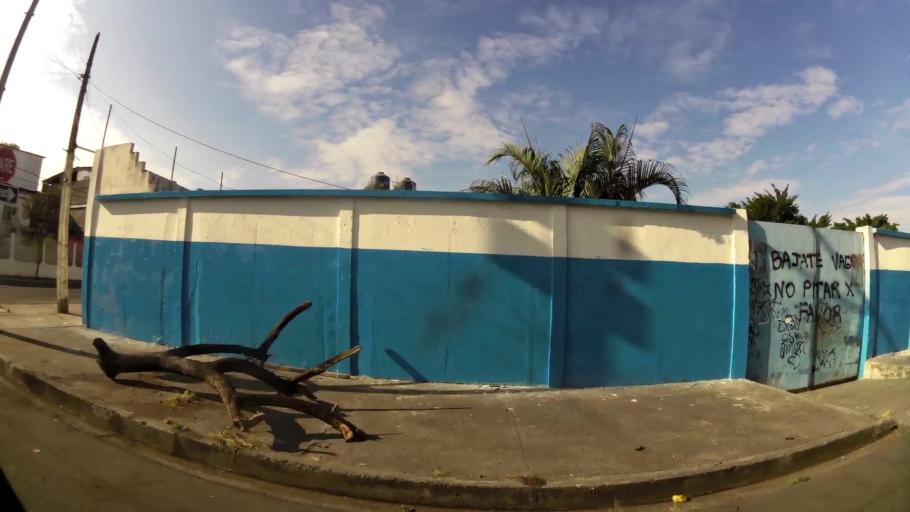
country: EC
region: Guayas
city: Guayaquil
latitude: -2.2189
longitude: -79.9194
